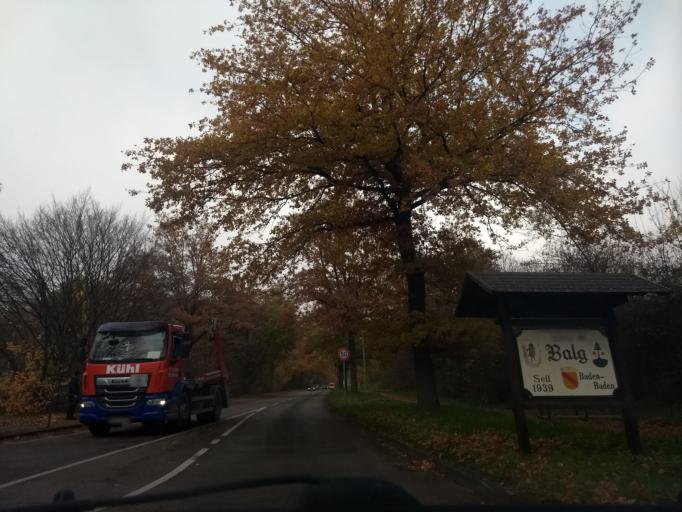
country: DE
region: Baden-Wuerttemberg
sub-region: Karlsruhe Region
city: Baden-Baden
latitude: 48.7841
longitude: 8.2110
